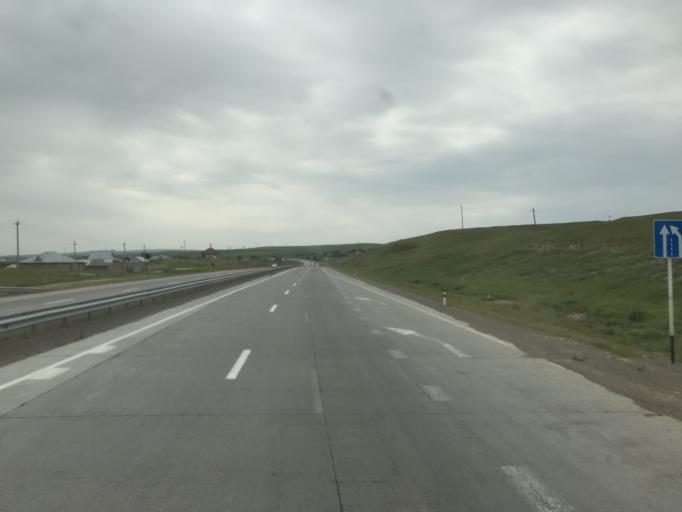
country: KZ
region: Ongtustik Qazaqstan
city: Qazyqurt
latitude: 41.8729
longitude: 69.4255
